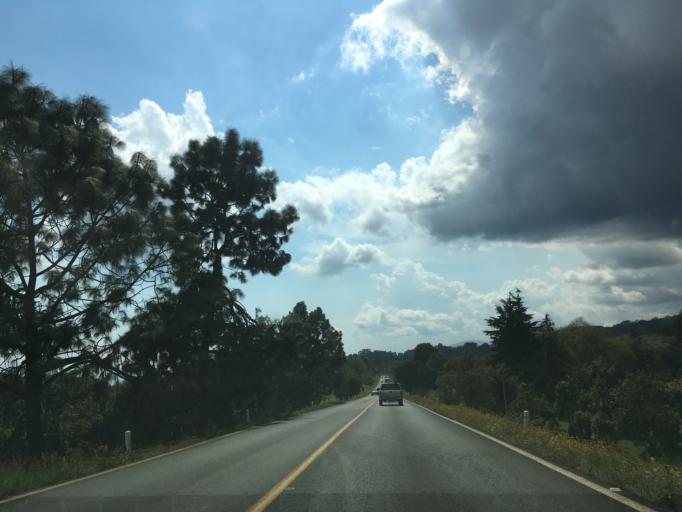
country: MX
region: Michoacan
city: Tingambato
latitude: 19.5045
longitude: -101.8634
